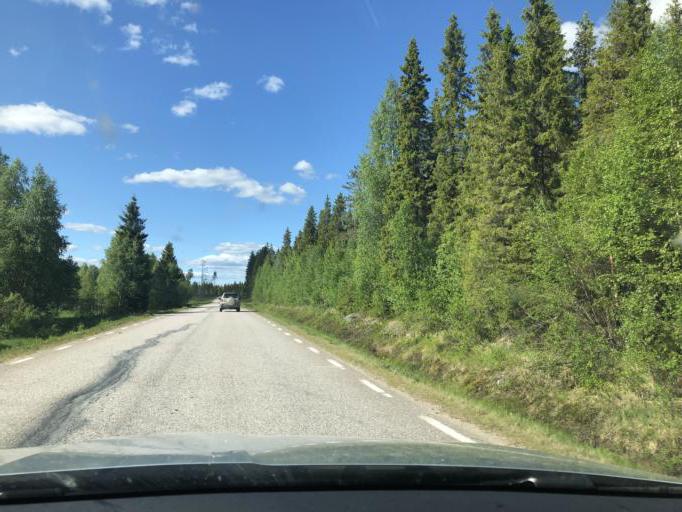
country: SE
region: Norrbotten
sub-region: Kalix Kommun
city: Kalix
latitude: 65.9480
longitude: 23.1521
